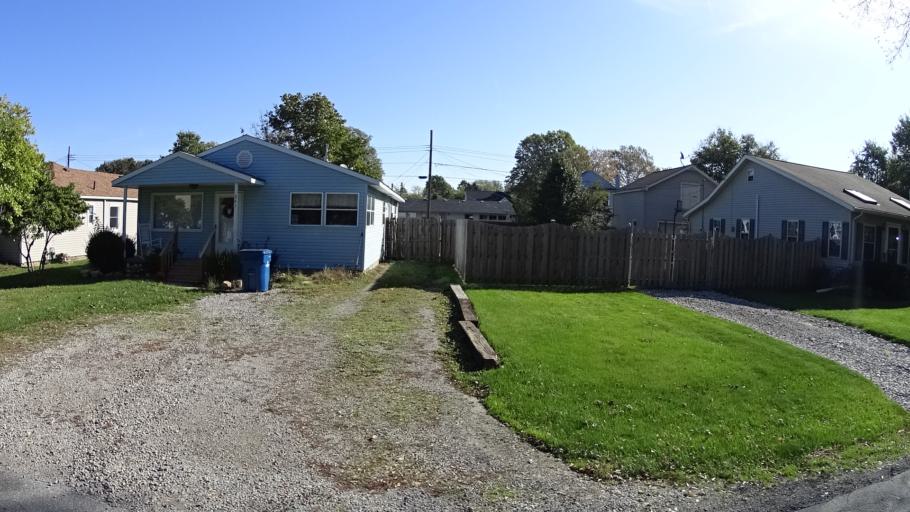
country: US
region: Ohio
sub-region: Lorain County
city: Vermilion-on-the-Lake
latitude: 41.4285
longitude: -82.3404
